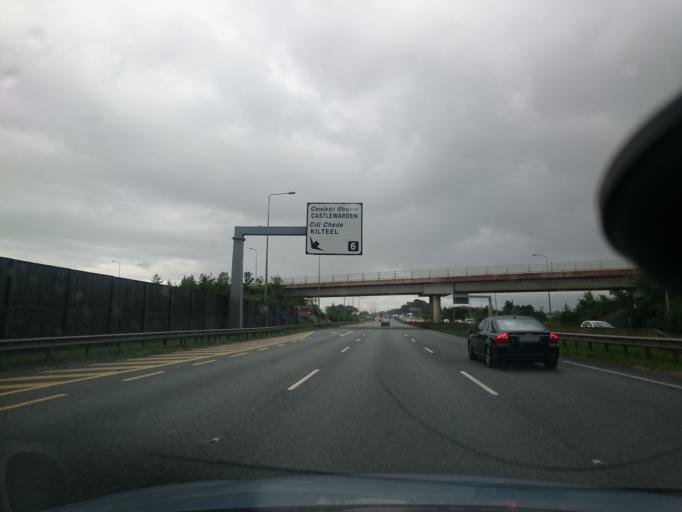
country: IE
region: Leinster
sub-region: Kildare
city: Kill
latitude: 53.2583
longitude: -6.5517
